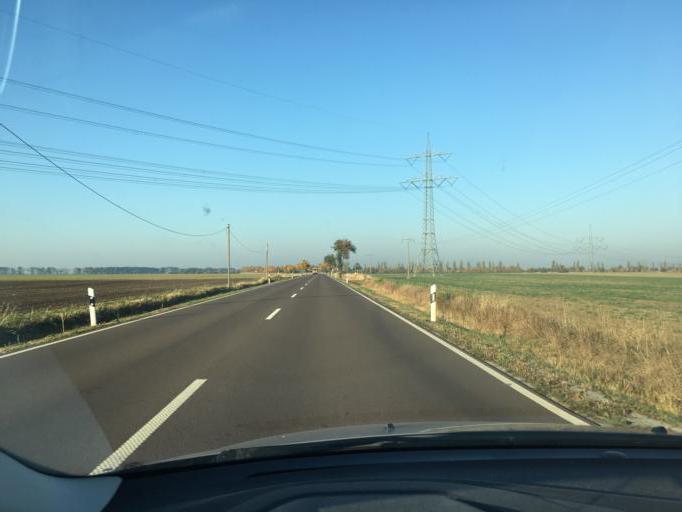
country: DE
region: Saxony-Anhalt
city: Welsleben
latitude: 52.0032
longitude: 11.6196
